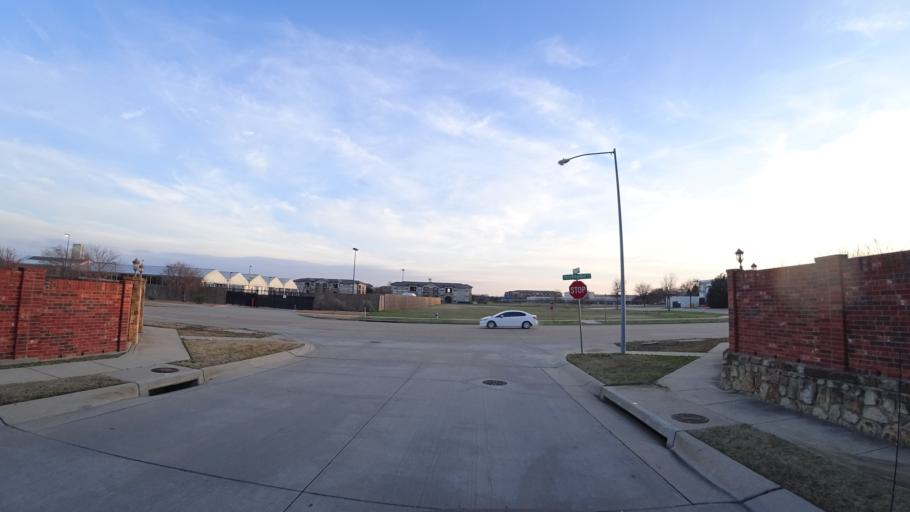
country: US
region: Texas
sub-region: Denton County
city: Lewisville
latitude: 32.9987
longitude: -96.9784
